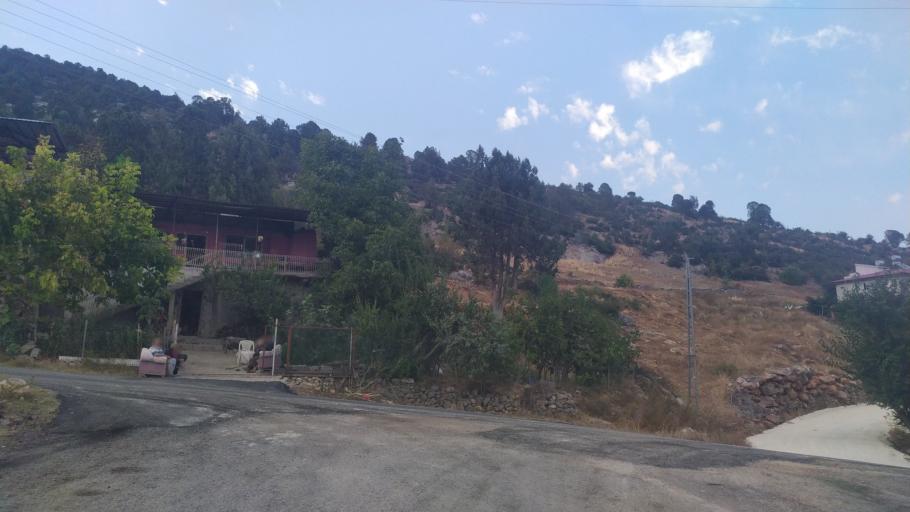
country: TR
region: Mersin
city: Camliyayla
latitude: 37.2303
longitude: 34.7100
